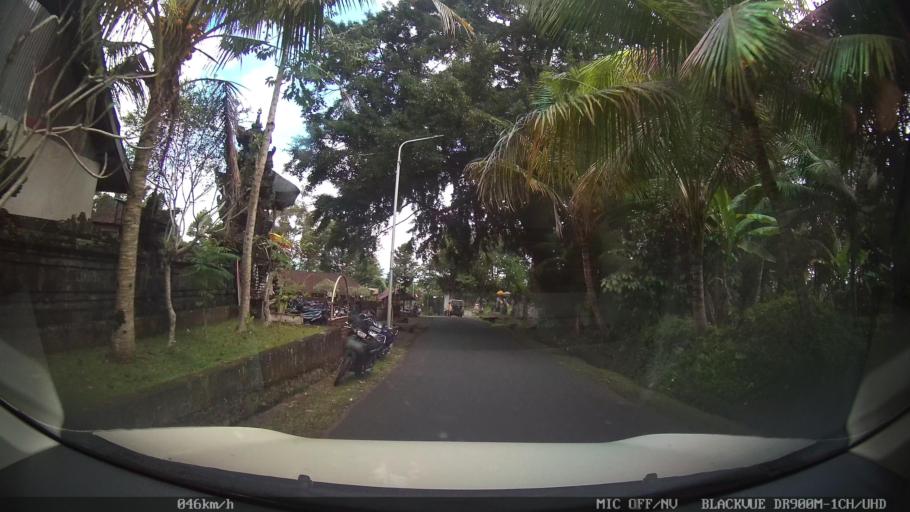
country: ID
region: Bali
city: Banjar Madangan Kaja
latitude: -8.4777
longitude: 115.3231
